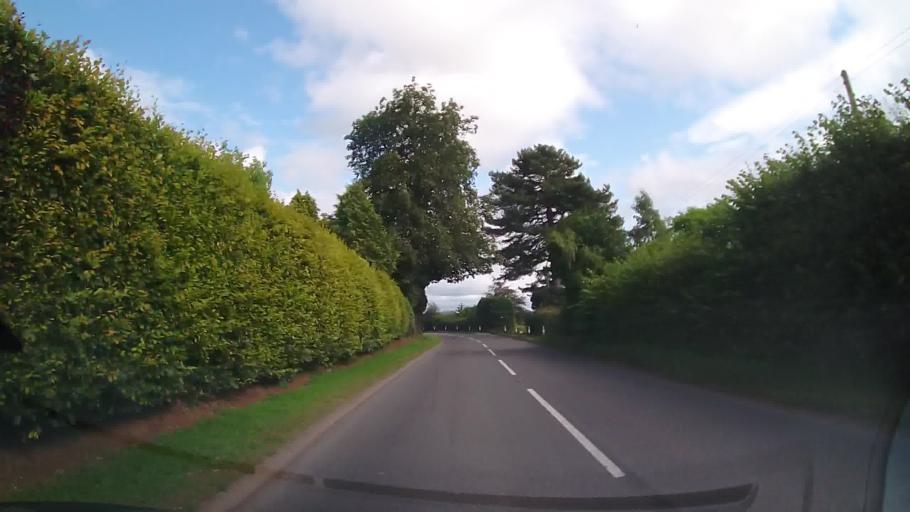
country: GB
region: England
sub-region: Shropshire
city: Pant
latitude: 52.8003
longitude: -3.0103
